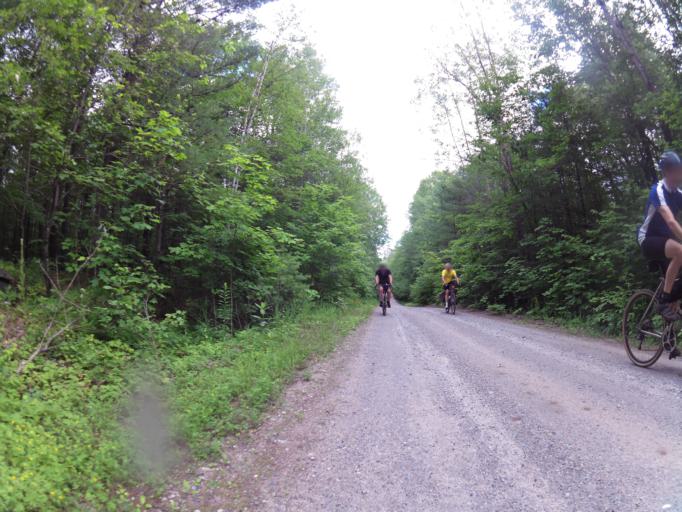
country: CA
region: Ontario
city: Perth
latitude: 45.0274
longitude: -76.5697
